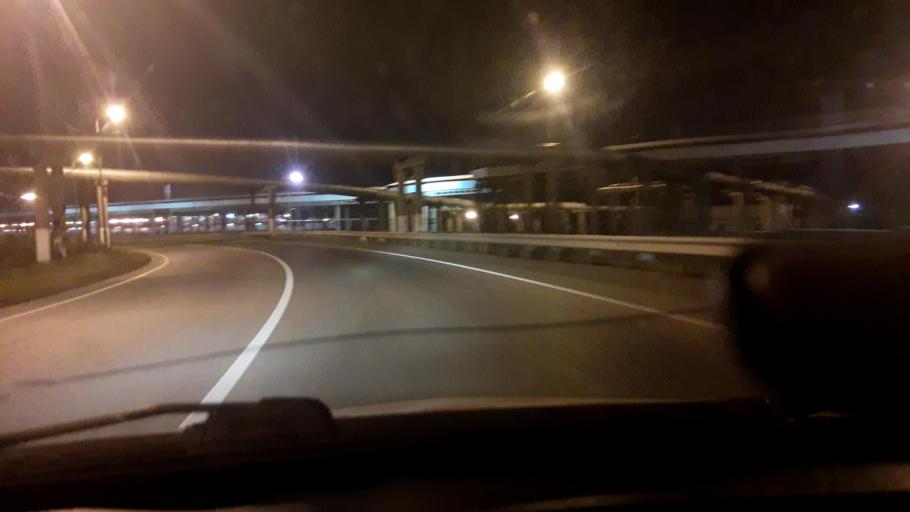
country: RU
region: Bashkortostan
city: Blagoveshchensk
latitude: 54.9176
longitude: 56.0658
